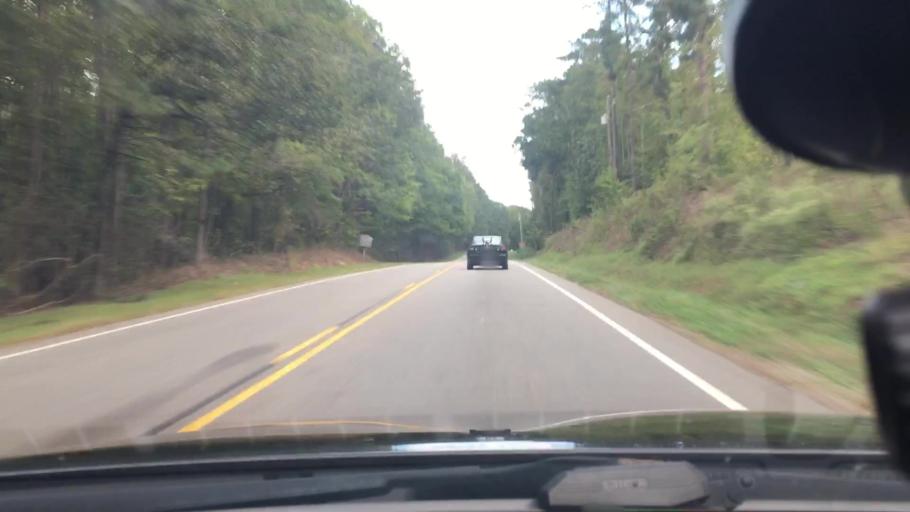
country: US
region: North Carolina
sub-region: Moore County
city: Carthage
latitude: 35.3601
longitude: -79.4369
